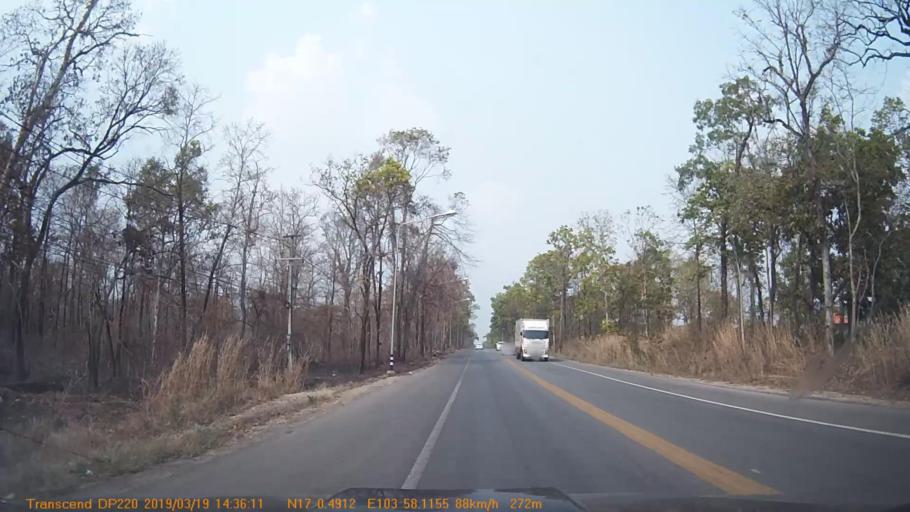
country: TH
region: Sakon Nakhon
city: Phu Phan
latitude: 17.0083
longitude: 103.9686
